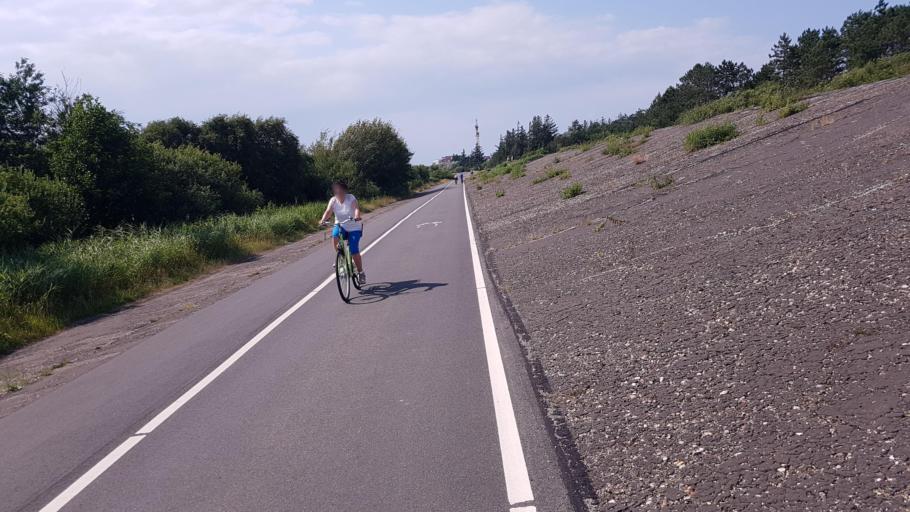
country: DE
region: Schleswig-Holstein
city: Sankt Peter-Ording
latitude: 54.3043
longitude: 8.6241
